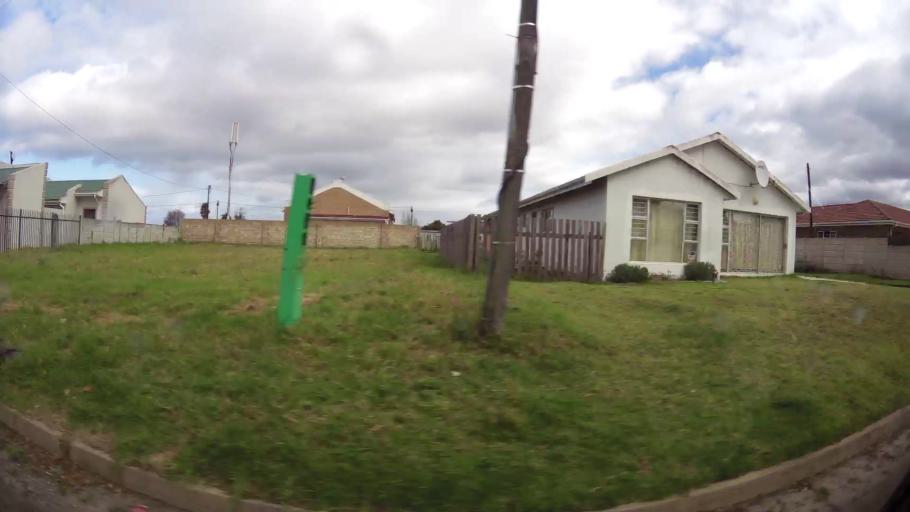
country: ZA
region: Western Cape
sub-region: Eden District Municipality
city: George
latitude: -33.9762
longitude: 22.4907
